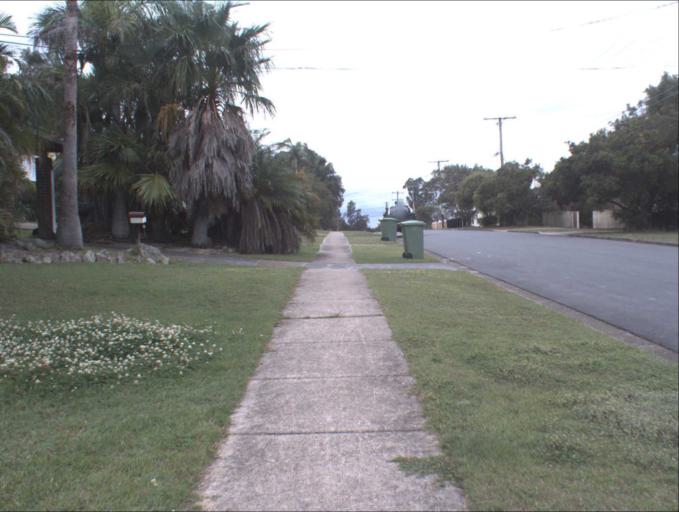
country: AU
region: Queensland
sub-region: Brisbane
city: Sunnybank Hills
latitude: -27.6623
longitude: 153.0334
